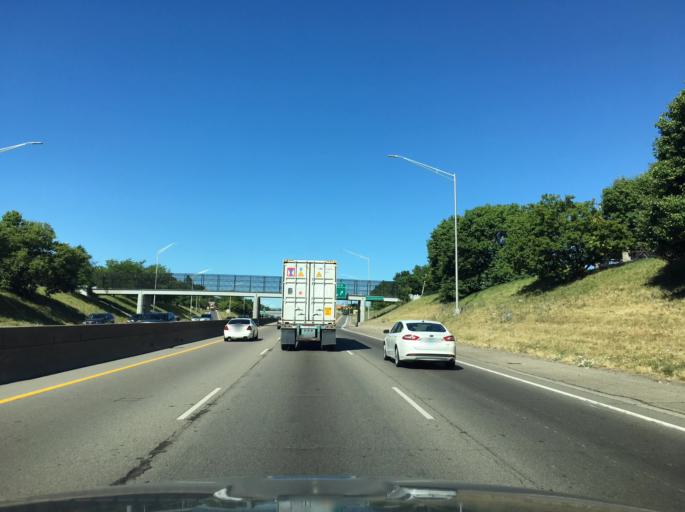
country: US
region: Michigan
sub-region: Wayne County
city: Grosse Pointe Park
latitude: 42.4065
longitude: -82.9554
